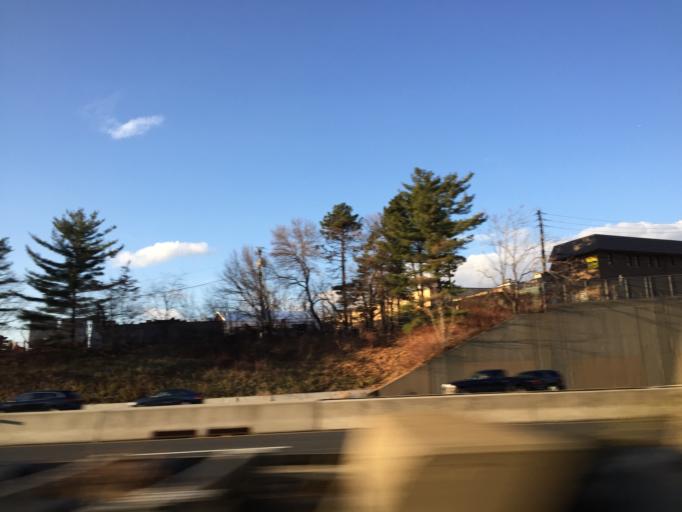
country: US
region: New Jersey
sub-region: Union County
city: Hillside
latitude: 40.7070
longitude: -74.2333
